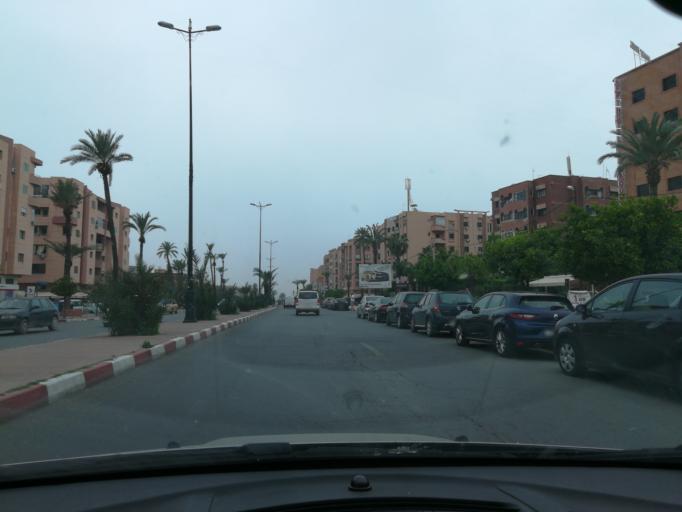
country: MA
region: Marrakech-Tensift-Al Haouz
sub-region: Marrakech
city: Marrakesh
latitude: 31.6517
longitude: -8.0163
